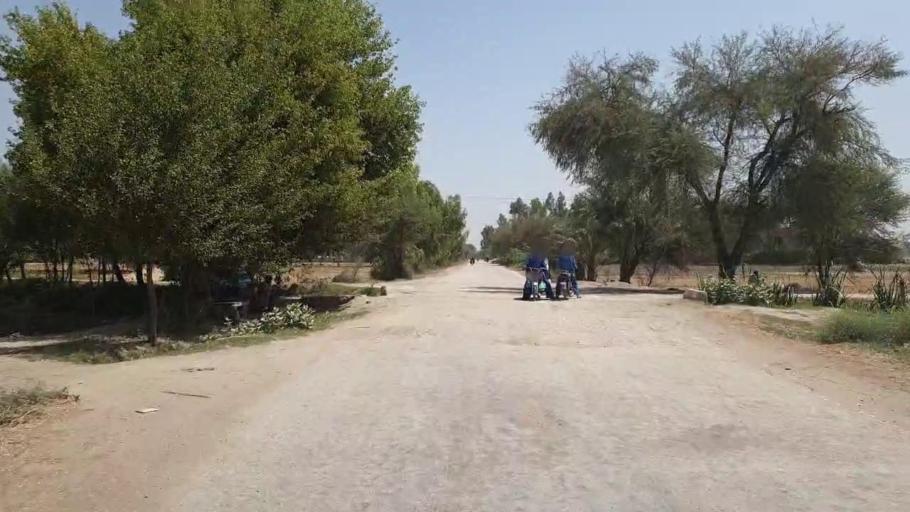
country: PK
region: Sindh
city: Adilpur
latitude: 27.8414
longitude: 69.2670
